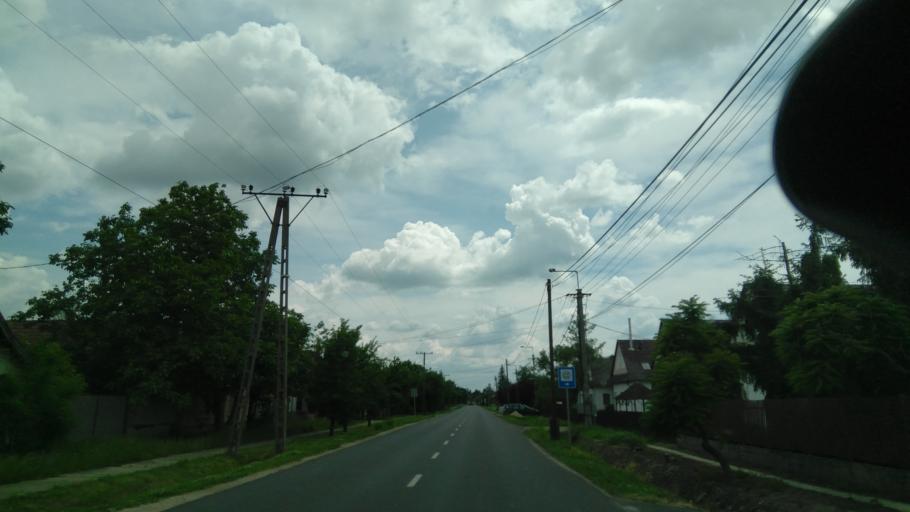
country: HU
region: Bekes
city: Totkomlos
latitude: 46.4212
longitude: 20.7330
